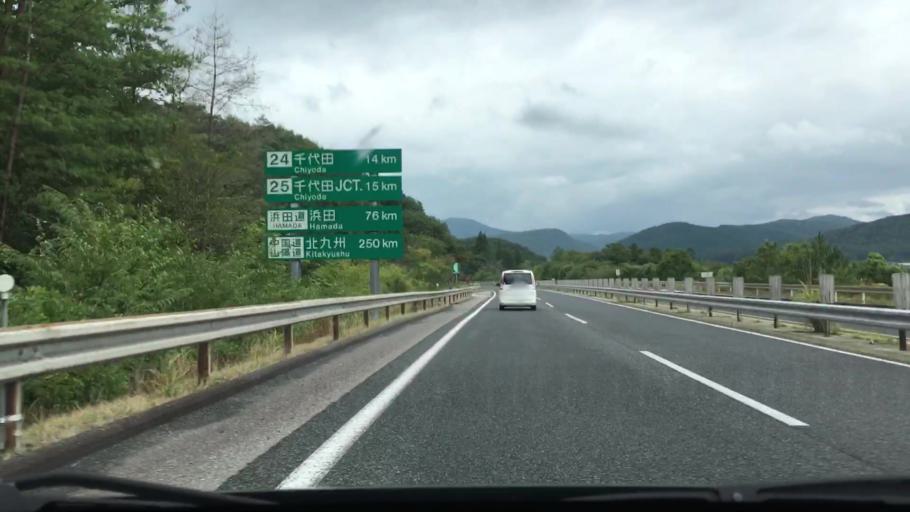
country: JP
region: Hiroshima
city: Miyoshi
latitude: 34.7179
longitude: 132.6674
